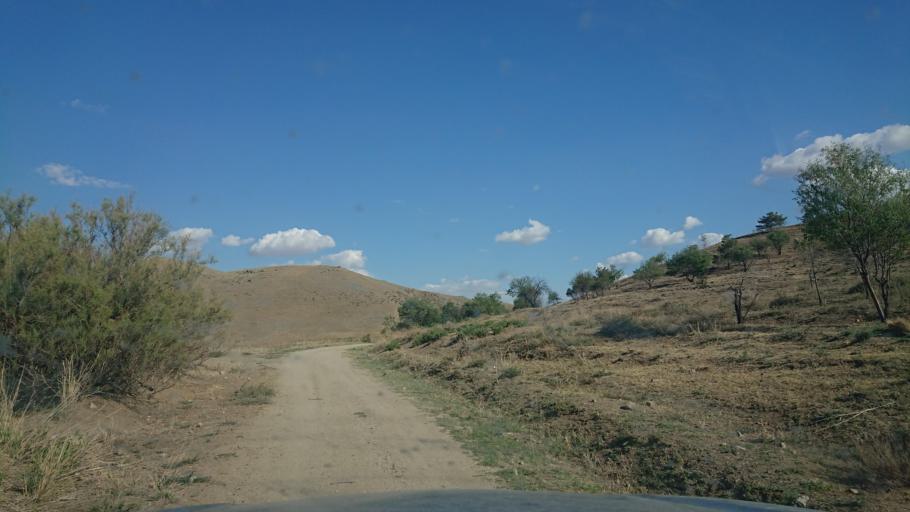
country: TR
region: Aksaray
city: Sariyahsi
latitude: 39.0221
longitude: 33.8955
